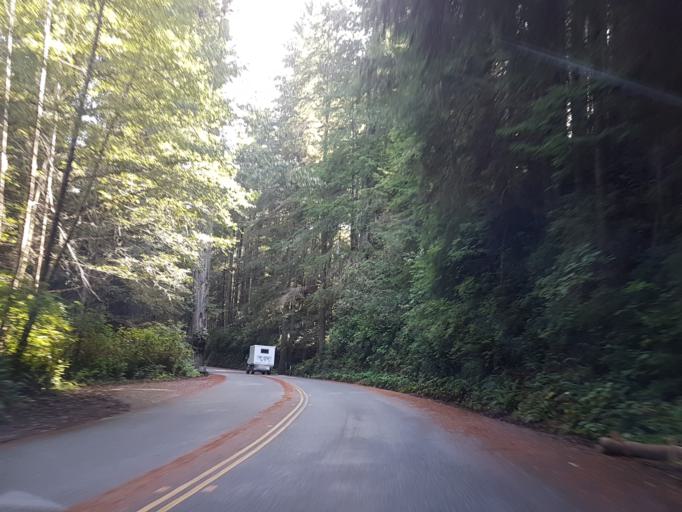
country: US
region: California
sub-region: Del Norte County
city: Bertsch-Oceanview
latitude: 41.4553
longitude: -124.0438
